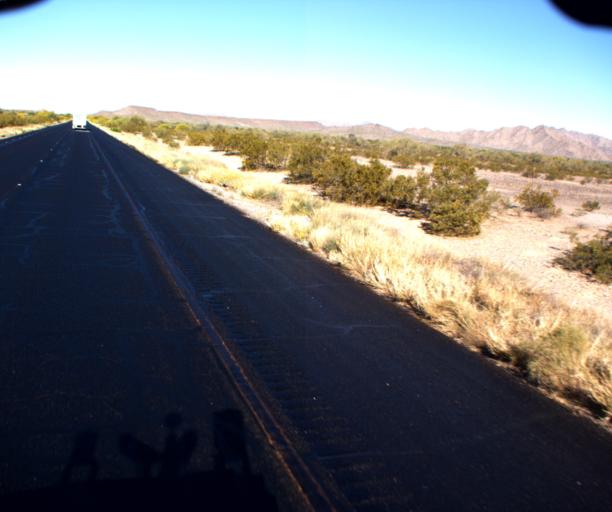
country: US
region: Arizona
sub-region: Pinal County
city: Maricopa
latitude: 32.8450
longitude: -112.2783
